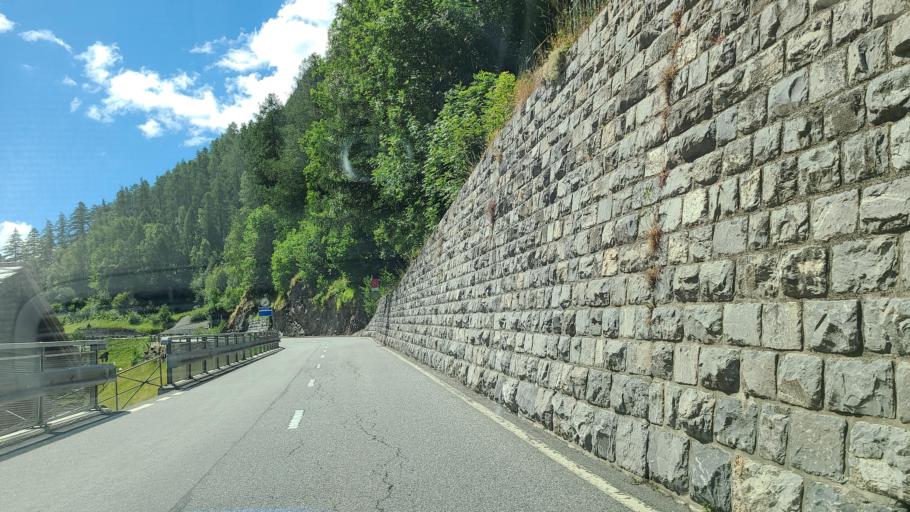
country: CH
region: Valais
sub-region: Visp District
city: Stalden
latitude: 46.1996
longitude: 7.8935
